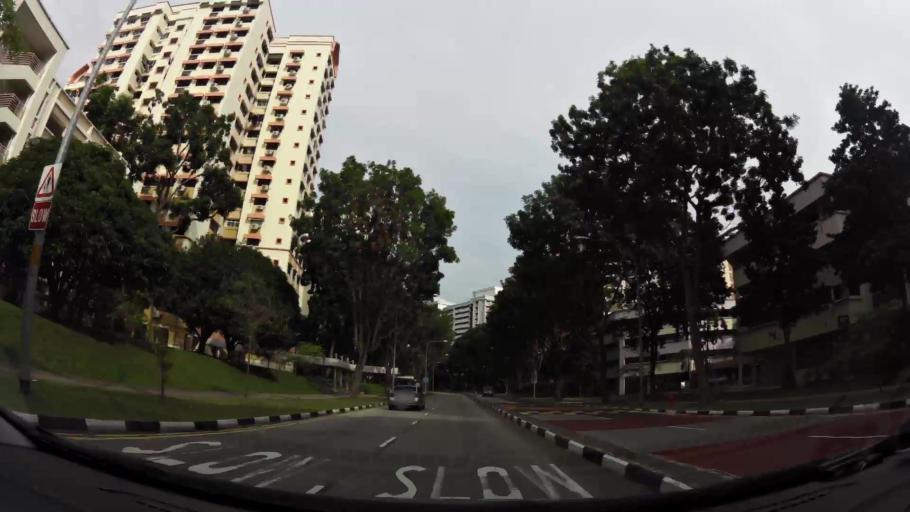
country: SG
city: Singapore
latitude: 1.3772
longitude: 103.8863
